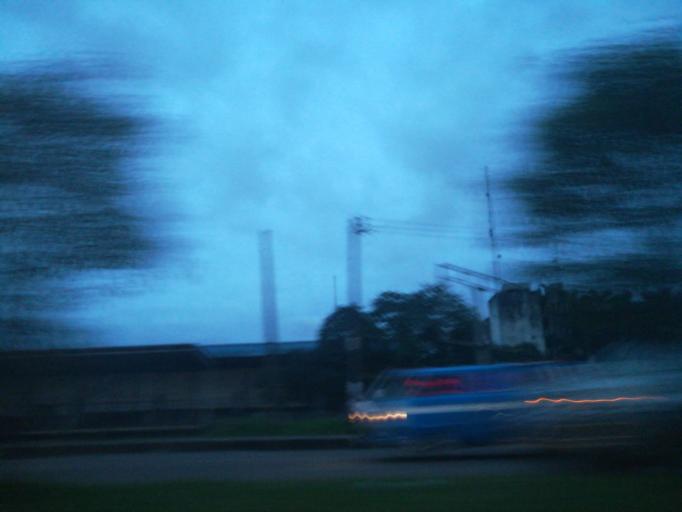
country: NG
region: Rivers
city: Port Harcourt
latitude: 4.7755
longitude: 7.0116
